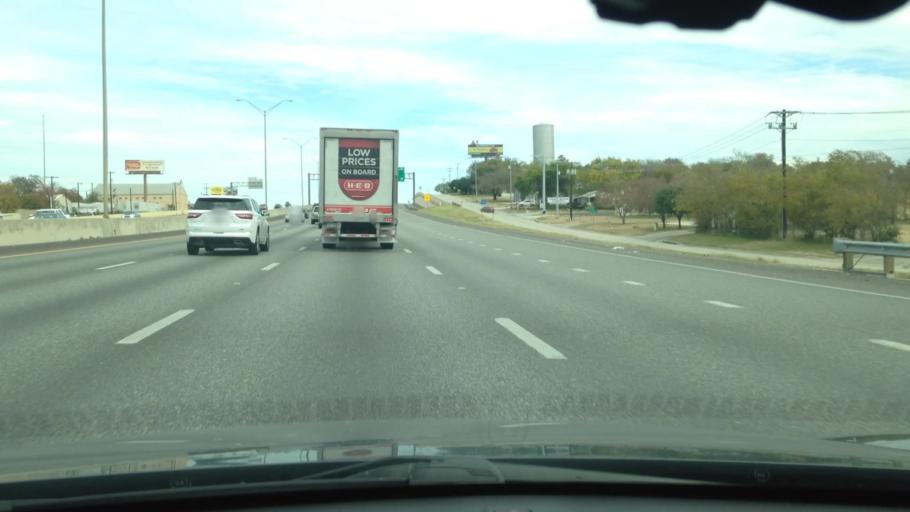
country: US
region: Texas
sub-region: Comal County
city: New Braunfels
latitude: 29.6774
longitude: -98.1499
